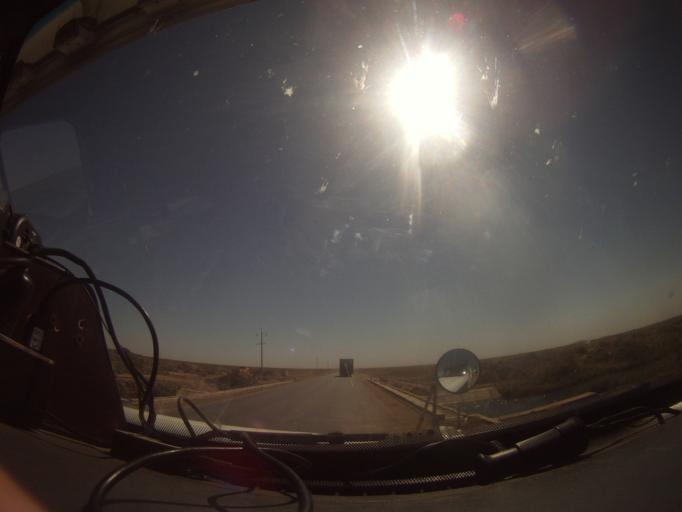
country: KZ
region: Qyzylorda
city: Dzhalagash
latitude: 45.0966
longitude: 64.2473
